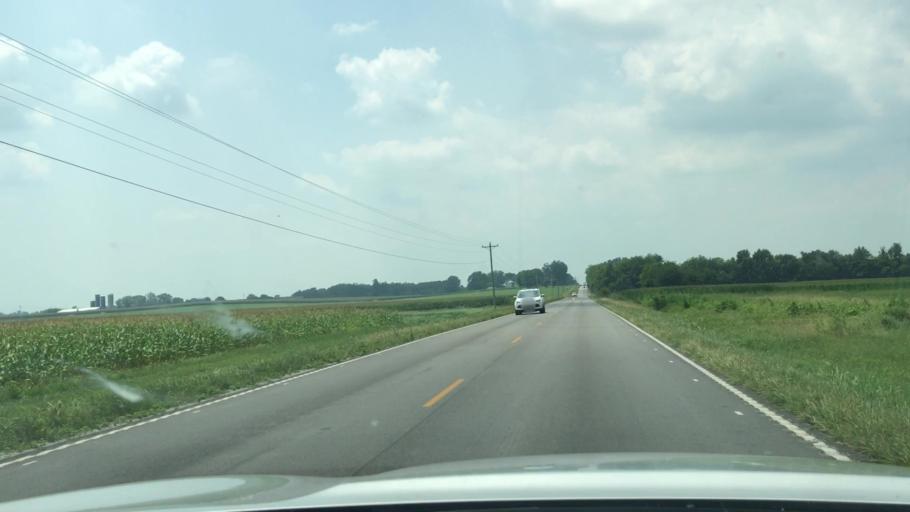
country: US
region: Kentucky
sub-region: Todd County
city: Guthrie
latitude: 36.6836
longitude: -87.1416
